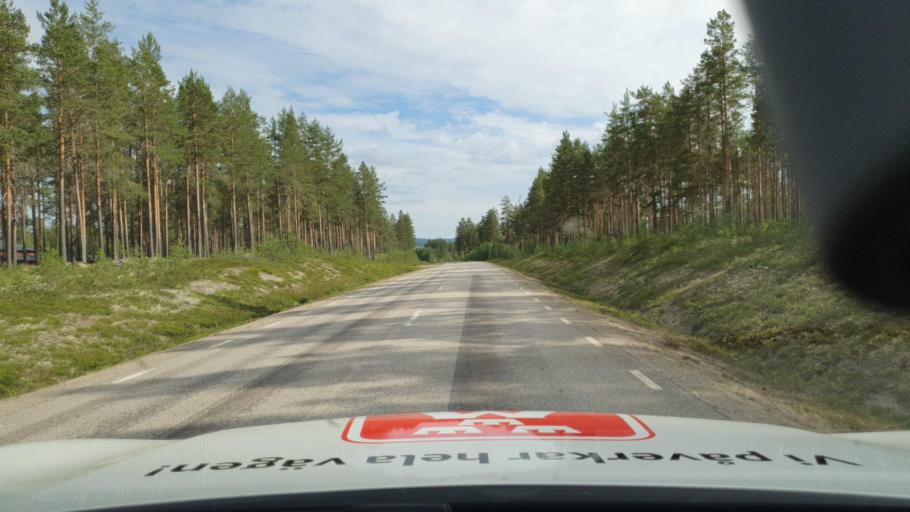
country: NO
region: Hedmark
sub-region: Trysil
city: Innbygda
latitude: 60.9488
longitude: 12.4692
